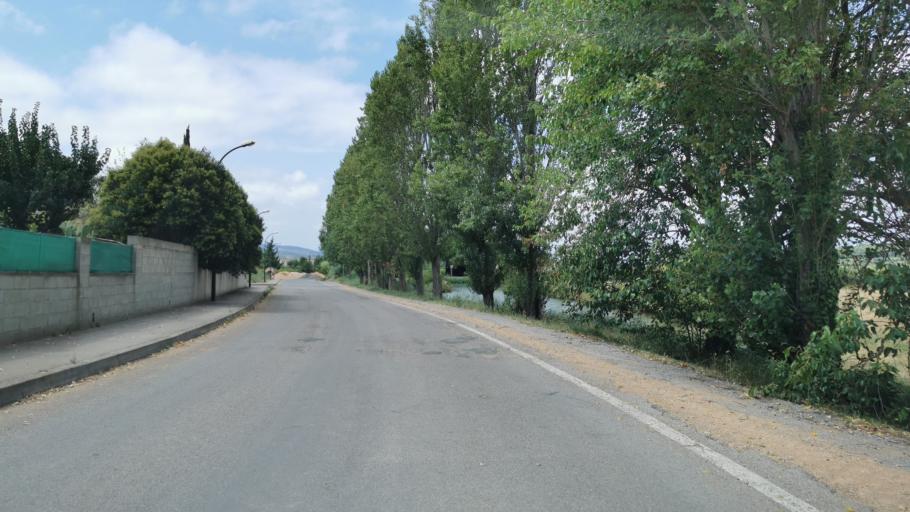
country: FR
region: Languedoc-Roussillon
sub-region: Departement de l'Aude
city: Bizanet
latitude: 43.1680
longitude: 2.8704
